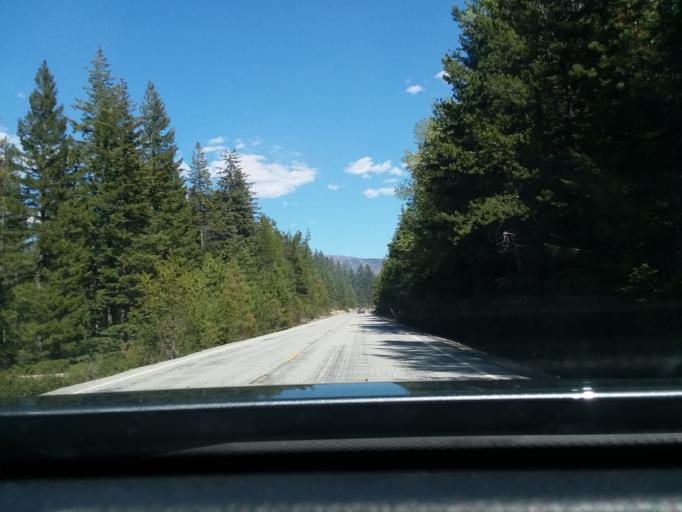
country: US
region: Washington
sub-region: Chelan County
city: Leavenworth
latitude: 47.8036
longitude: -120.6996
